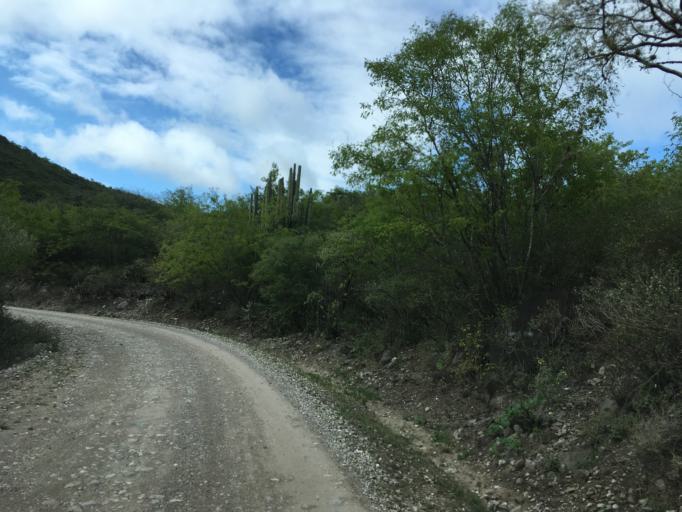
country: MX
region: Hidalgo
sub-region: Metztitlan
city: Fontezuelas
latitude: 20.6424
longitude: -98.9390
